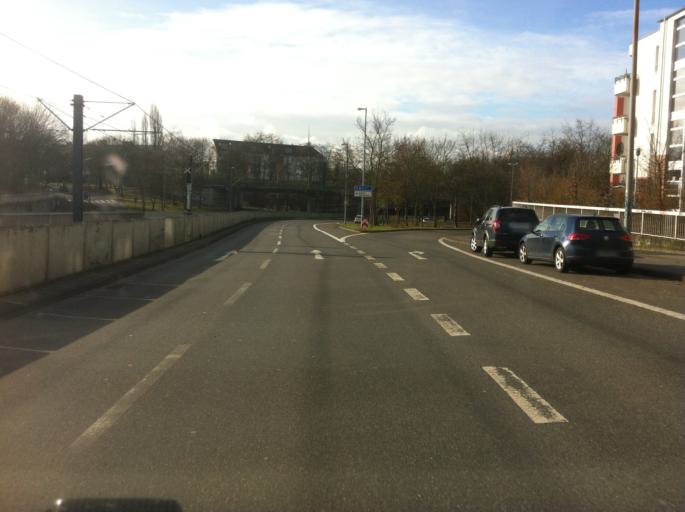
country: DE
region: North Rhine-Westphalia
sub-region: Regierungsbezirk Koln
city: Nippes
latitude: 50.9701
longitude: 6.9434
